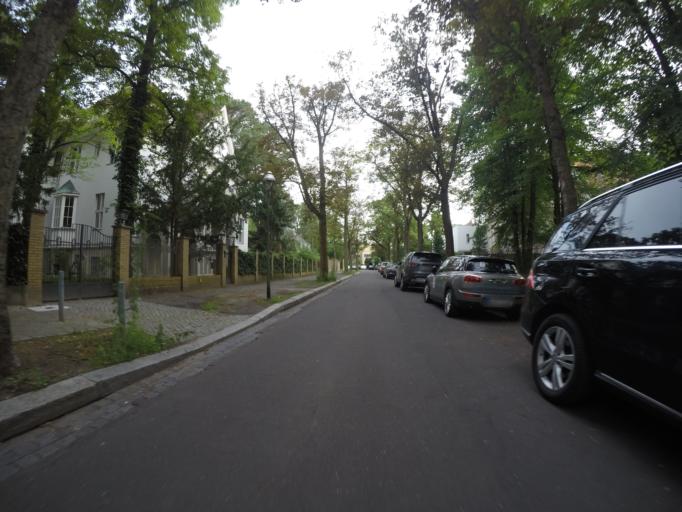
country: DE
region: Berlin
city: Grunewald
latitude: 52.4812
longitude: 13.2642
